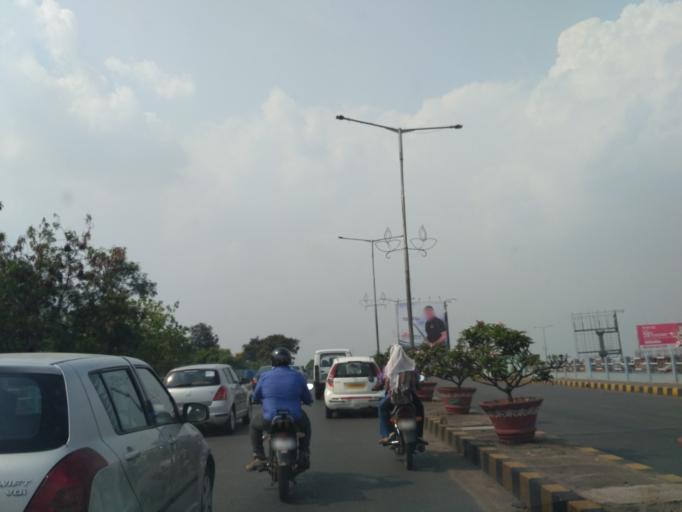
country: IN
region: Telangana
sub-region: Hyderabad
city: Hyderabad
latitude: 17.4145
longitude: 78.4608
